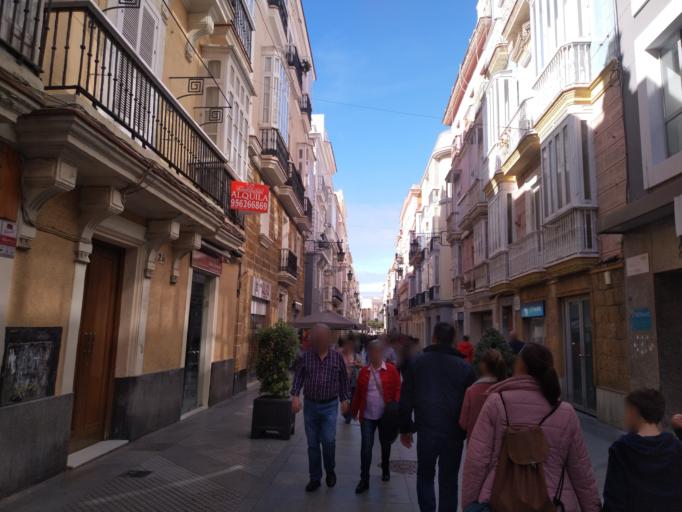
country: ES
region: Andalusia
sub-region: Provincia de Cadiz
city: Cadiz
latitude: 36.5334
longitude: -6.2974
